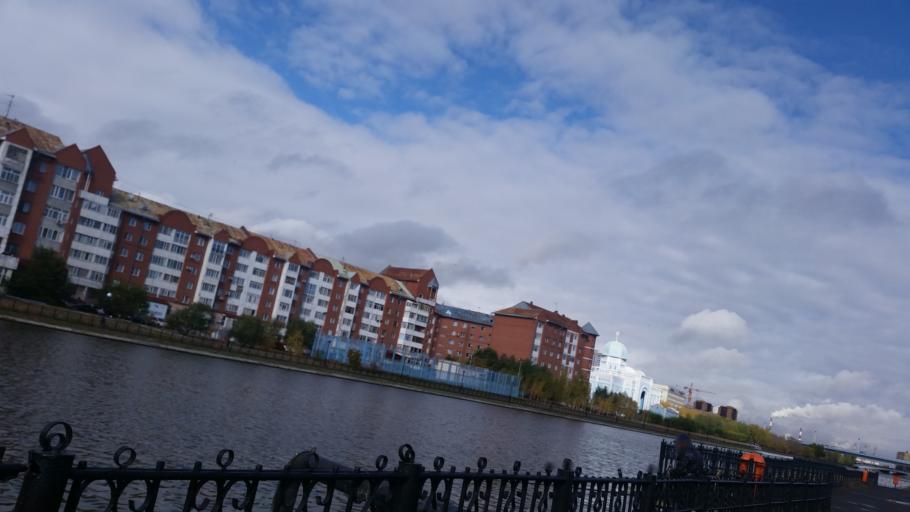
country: KZ
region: Astana Qalasy
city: Astana
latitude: 51.1552
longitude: 71.4595
